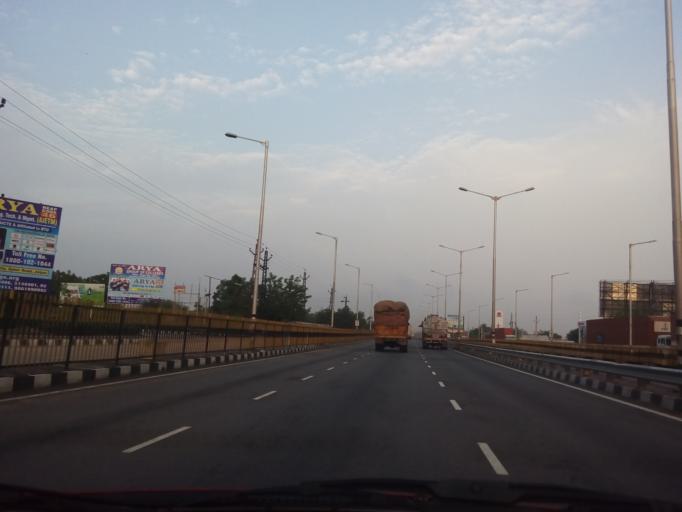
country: IN
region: Rajasthan
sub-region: Jaipur
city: Jaipur
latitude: 26.8486
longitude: 75.6324
